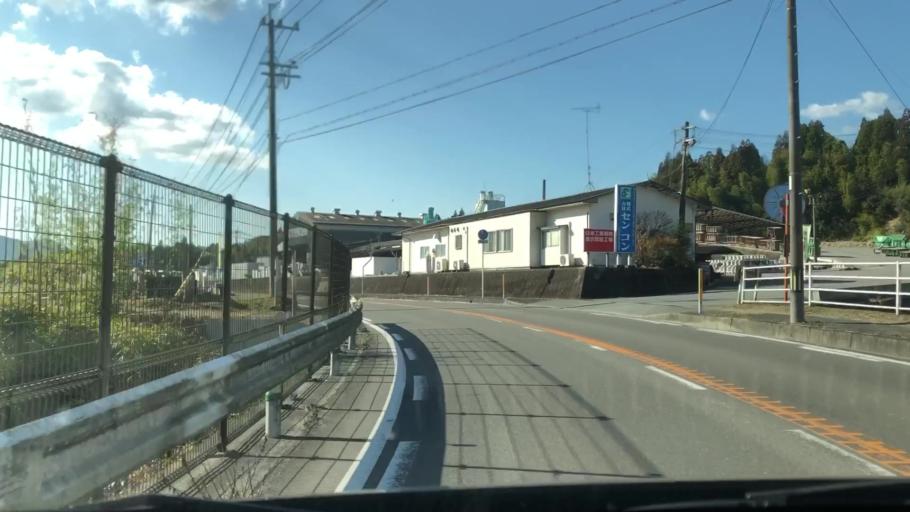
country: JP
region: Kagoshima
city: Satsumasendai
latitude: 31.8588
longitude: 130.3707
